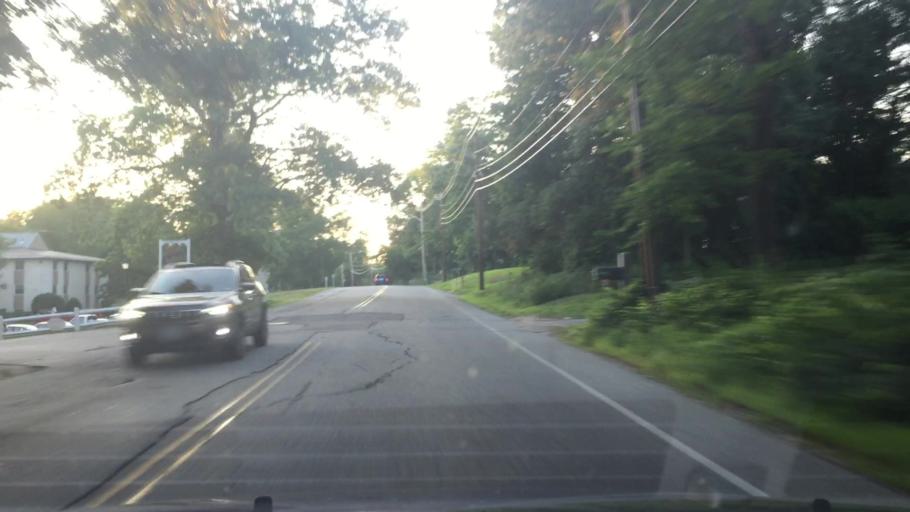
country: US
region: New Hampshire
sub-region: Rockingham County
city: Plaistow
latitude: 42.8095
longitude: -71.0881
